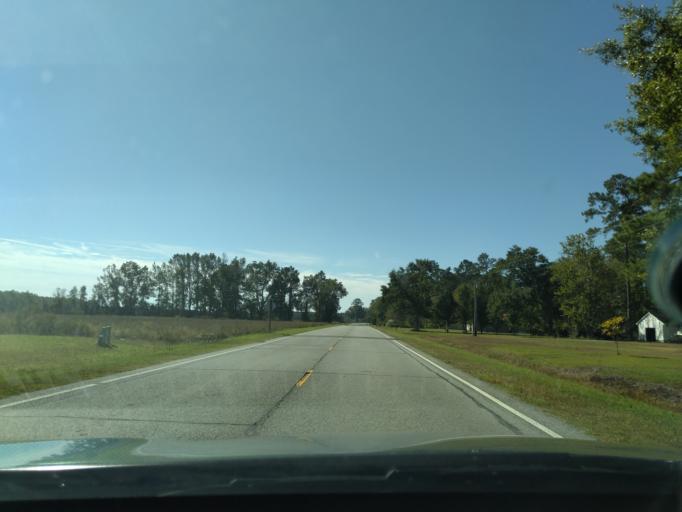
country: US
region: North Carolina
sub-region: Beaufort County
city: Belhaven
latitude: 35.6247
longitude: -76.8098
